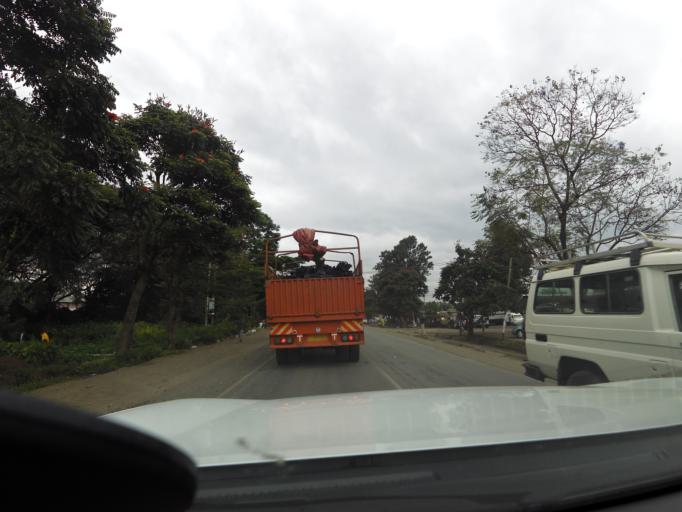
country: TZ
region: Arusha
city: Arusha
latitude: -3.3627
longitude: 36.6789
